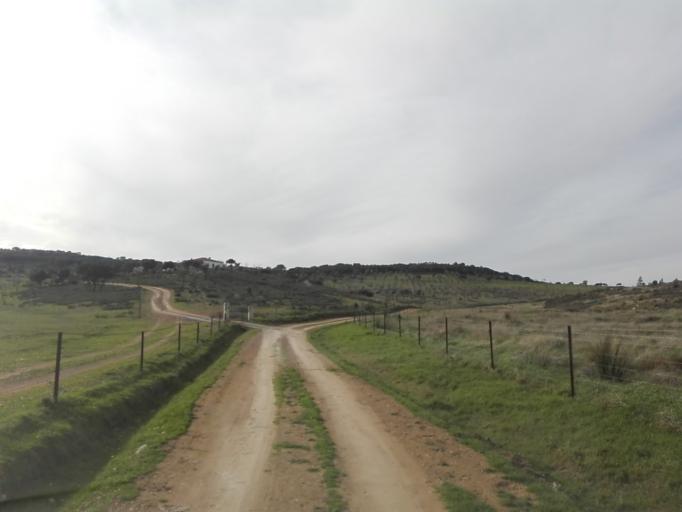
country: ES
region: Extremadura
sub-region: Provincia de Badajoz
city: Llerena
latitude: 38.2162
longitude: -6.0358
